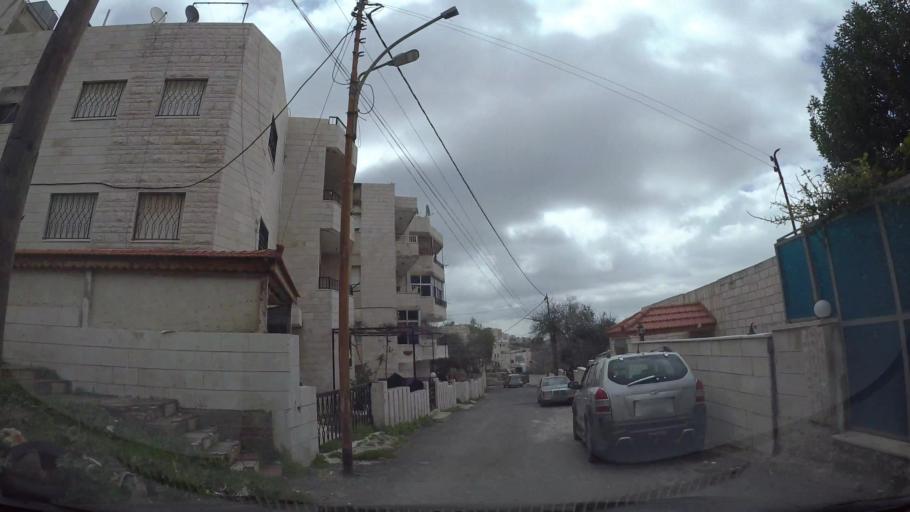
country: JO
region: Amman
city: Wadi as Sir
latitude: 31.9469
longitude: 35.8247
